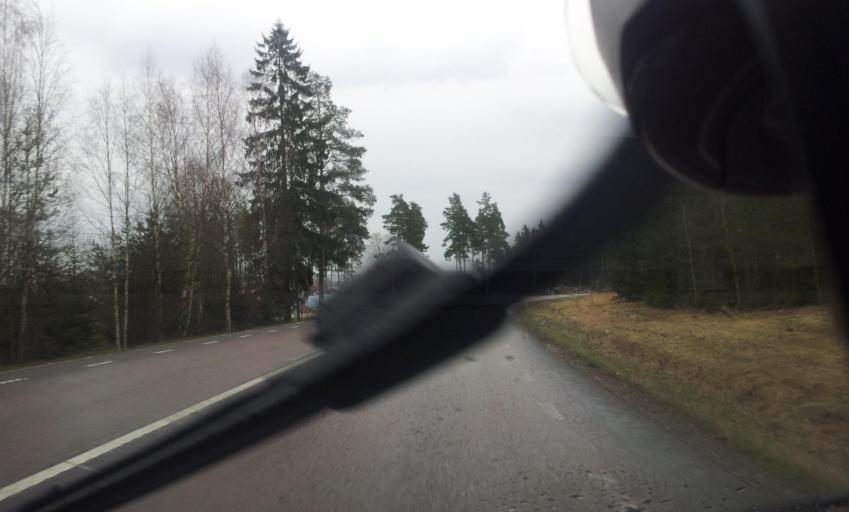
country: SE
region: Dalarna
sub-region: Borlange Kommun
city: Borlaenge
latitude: 60.5284
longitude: 15.3428
